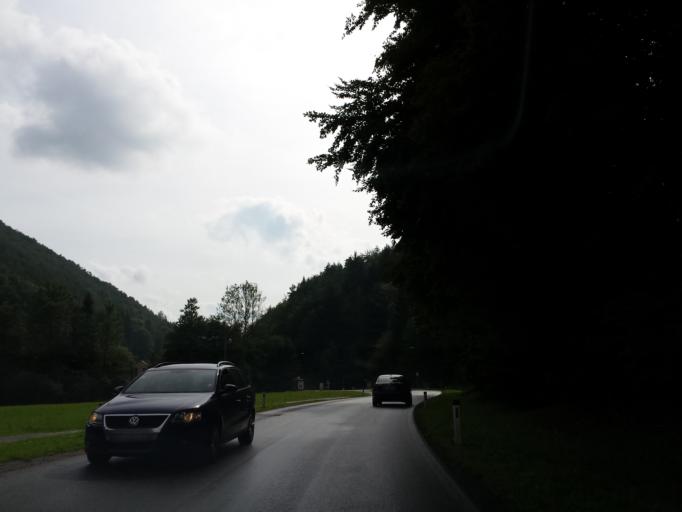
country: AT
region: Styria
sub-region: Politischer Bezirk Graz-Umgebung
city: Thal
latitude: 47.0887
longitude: 15.3729
